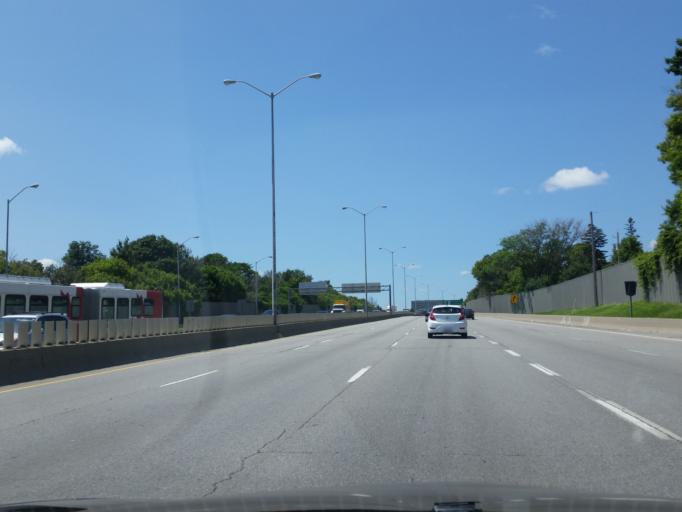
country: CA
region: Ontario
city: Ottawa
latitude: 45.4151
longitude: -75.6770
